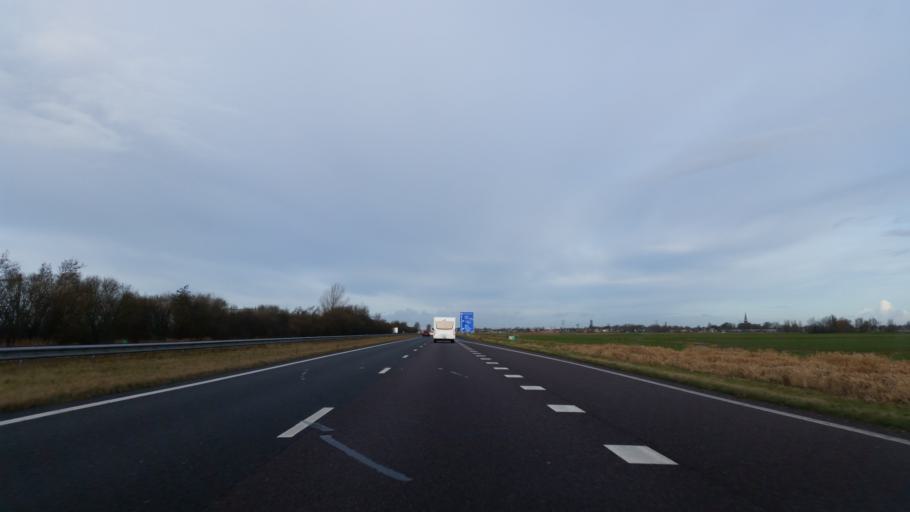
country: NL
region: Friesland
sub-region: Gemeente Leeuwarden
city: Wirdum
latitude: 53.1336
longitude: 5.8016
